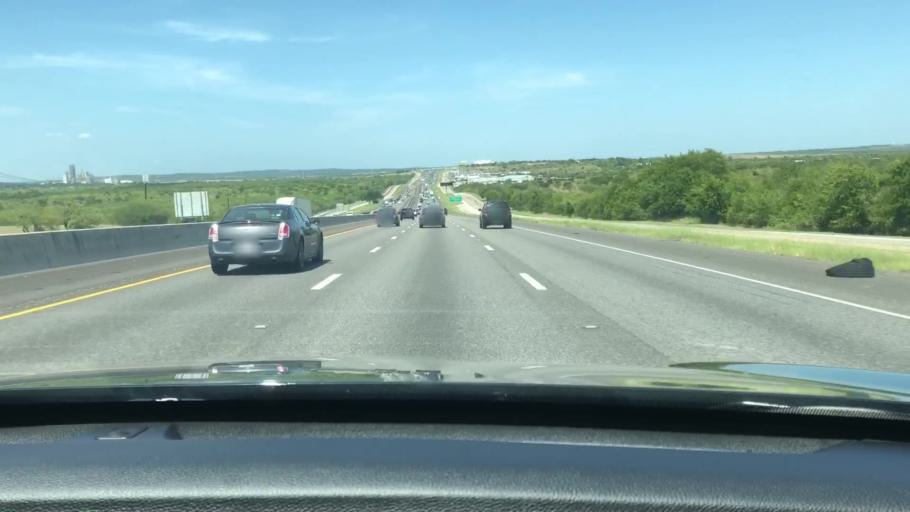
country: US
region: Texas
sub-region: Guadalupe County
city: Lake Dunlap
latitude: 29.7586
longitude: -98.0483
